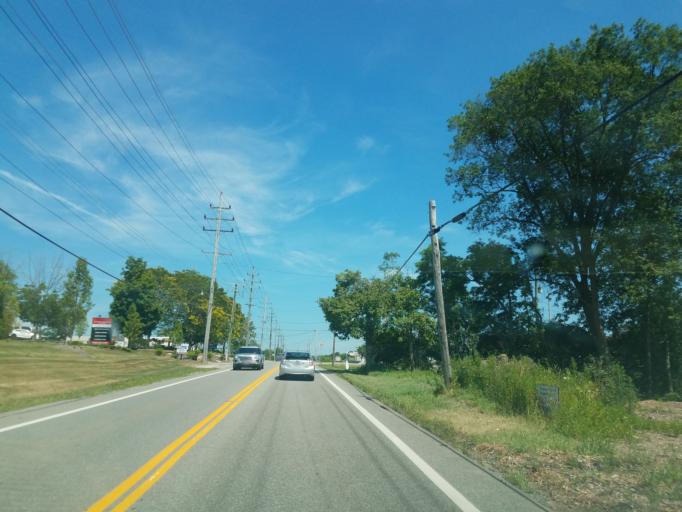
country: US
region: Ohio
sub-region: Geauga County
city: Chesterland
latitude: 41.5224
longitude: -81.3572
